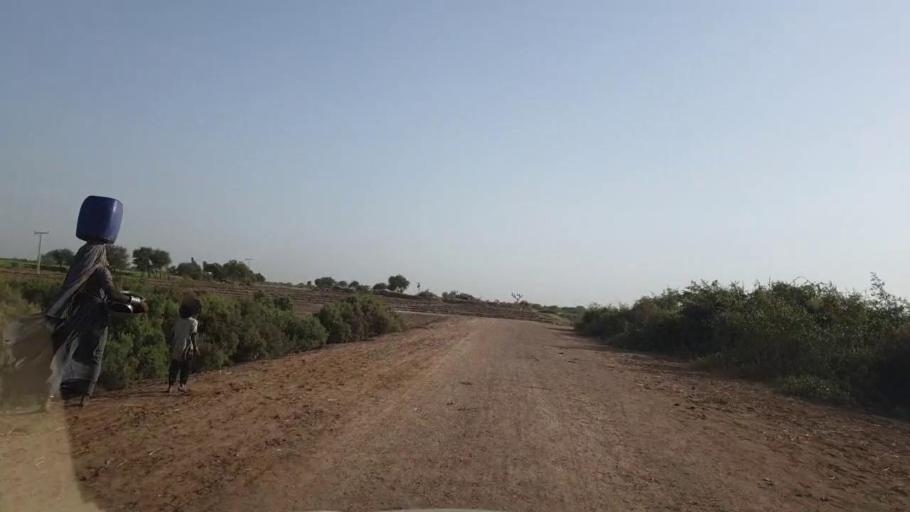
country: PK
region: Sindh
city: Tando Ghulam Ali
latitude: 25.0667
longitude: 68.8918
